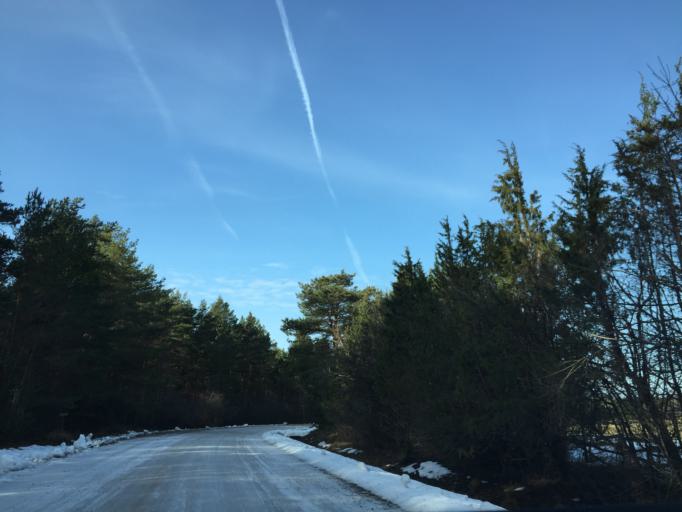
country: EE
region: Saare
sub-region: Kuressaare linn
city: Kuressaare
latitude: 58.3677
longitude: 22.0241
